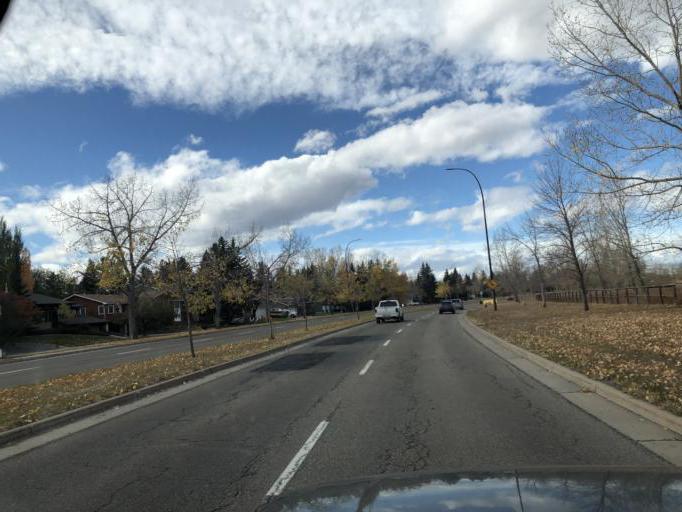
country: CA
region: Alberta
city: Calgary
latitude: 50.9723
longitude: -114.1207
